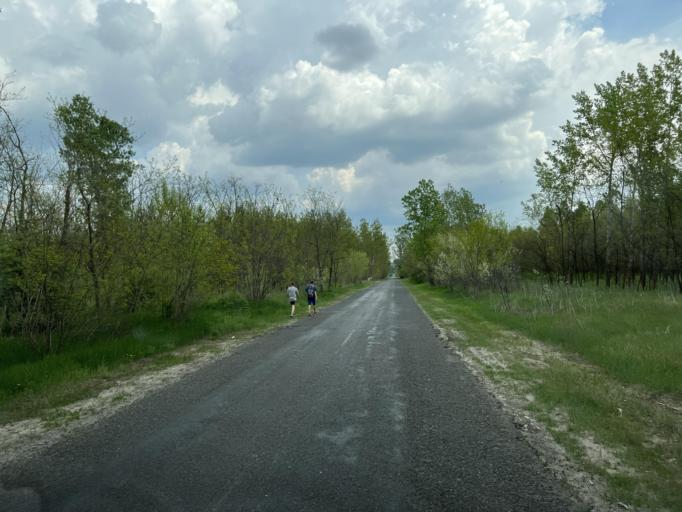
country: HU
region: Pest
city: Csemo
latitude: 47.0983
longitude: 19.7411
